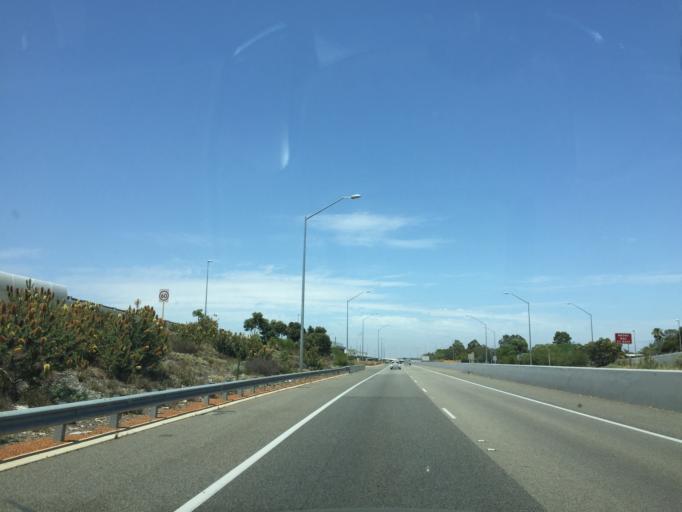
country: AU
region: Western Australia
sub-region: Belmont
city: Kewdale
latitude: -31.9742
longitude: 115.9488
